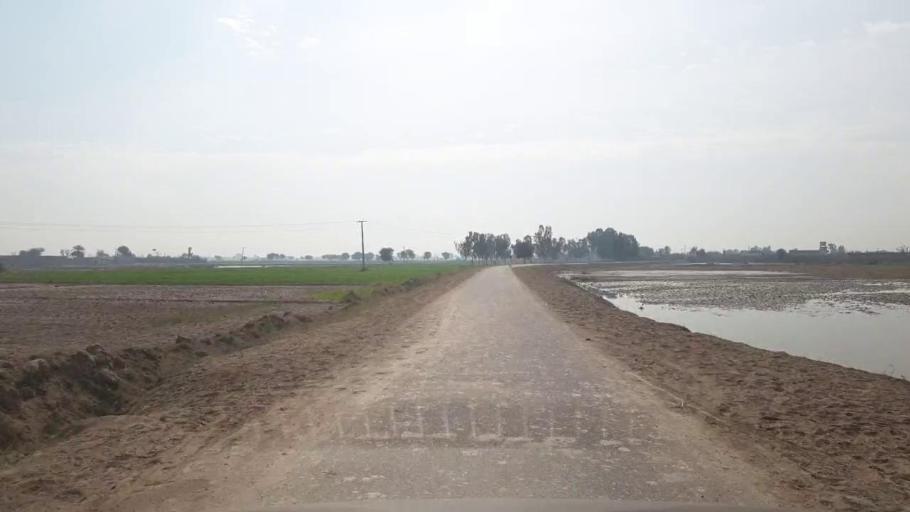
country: PK
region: Sindh
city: Hala
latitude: 25.9911
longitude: 68.4221
